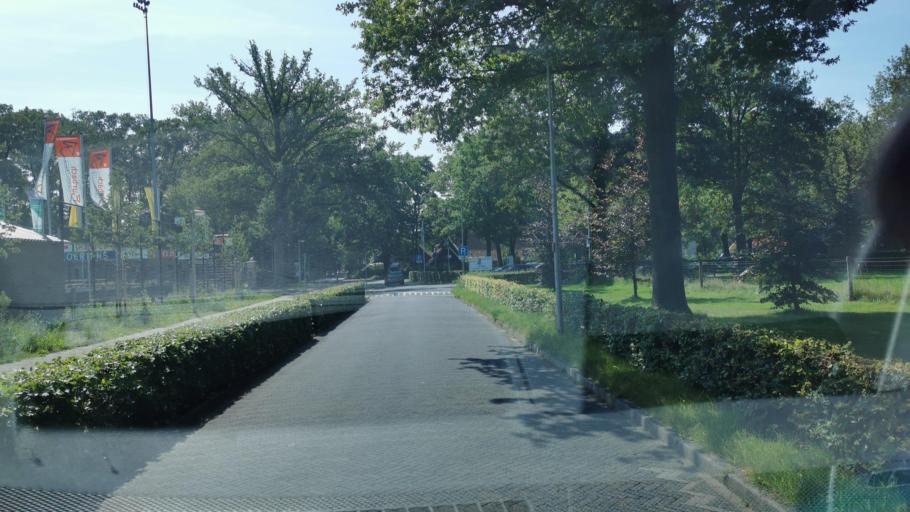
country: NL
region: Overijssel
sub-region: Gemeente Haaksbergen
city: Haaksbergen
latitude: 52.1479
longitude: 6.7272
